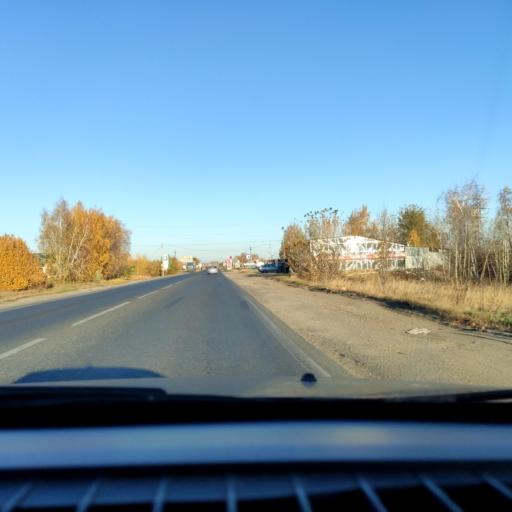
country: RU
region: Samara
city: Tol'yatti
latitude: 53.5635
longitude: 49.3538
